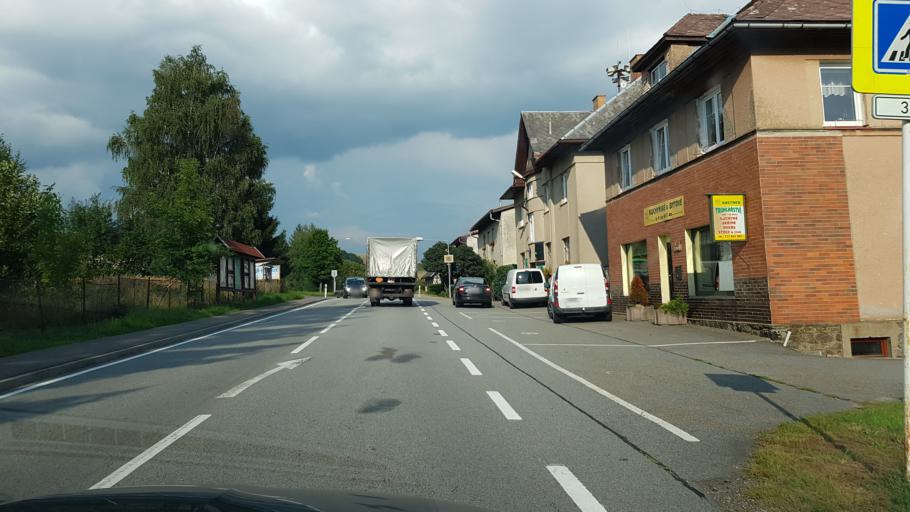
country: PL
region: Lower Silesian Voivodeship
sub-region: Powiat klodzki
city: Miedzylesie
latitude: 50.0969
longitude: 16.6622
